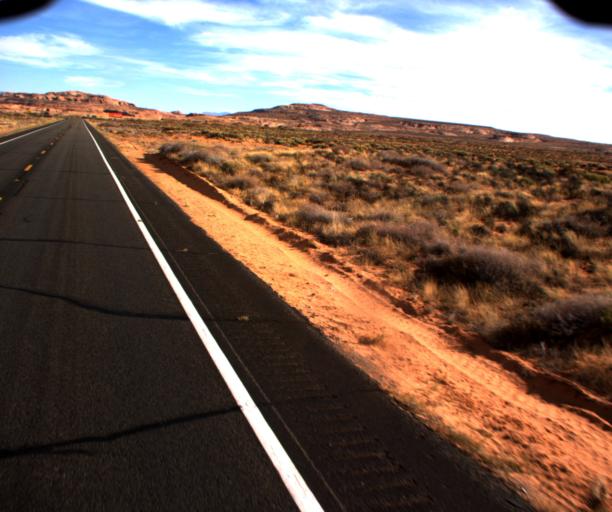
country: US
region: Arizona
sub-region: Apache County
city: Many Farms
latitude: 36.9282
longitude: -109.6203
